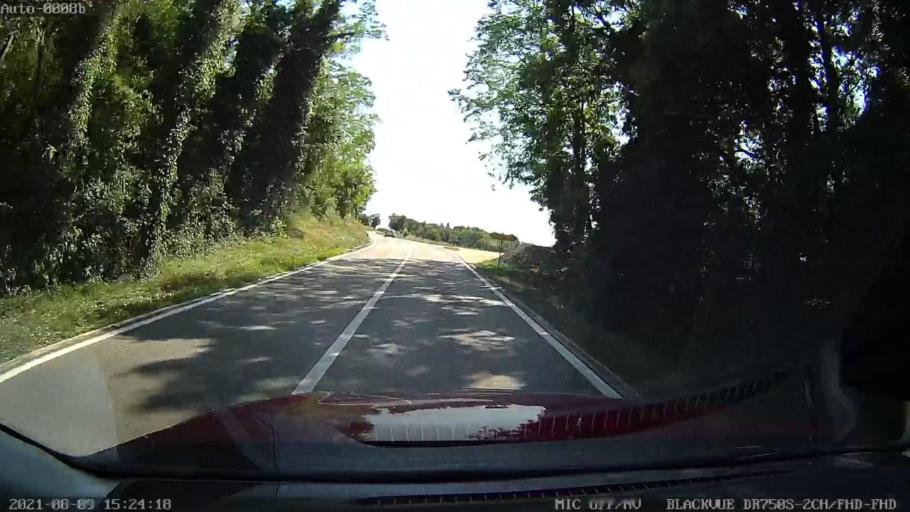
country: HR
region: Istarska
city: Pazin
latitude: 45.1765
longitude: 13.9037
